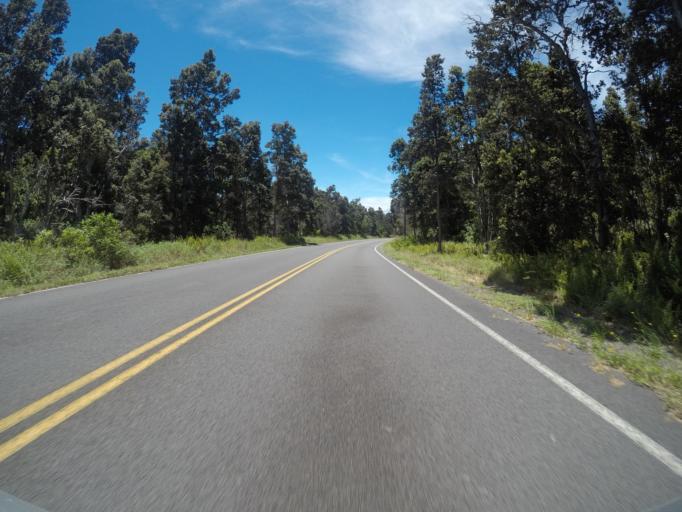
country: US
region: Hawaii
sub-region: Hawaii County
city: Volcano
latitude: 19.3558
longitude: -155.2230
